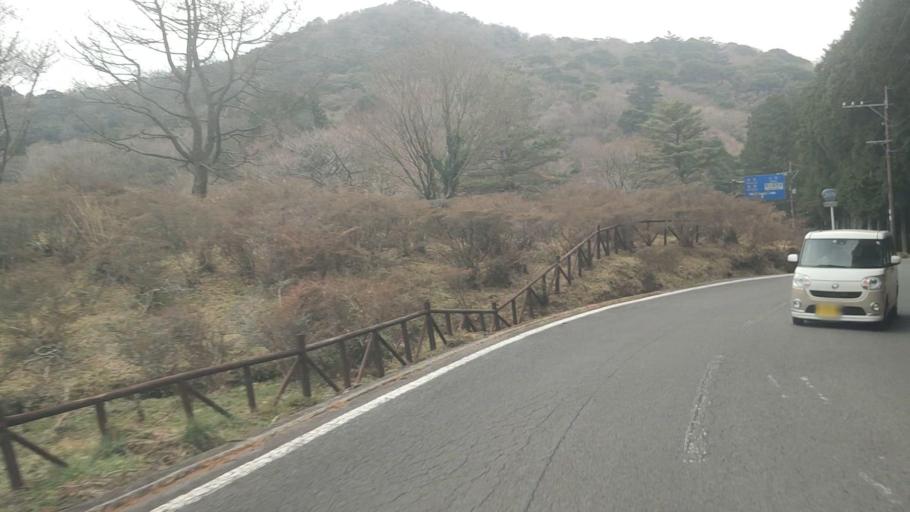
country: JP
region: Nagasaki
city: Shimabara
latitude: 32.7449
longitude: 130.2688
